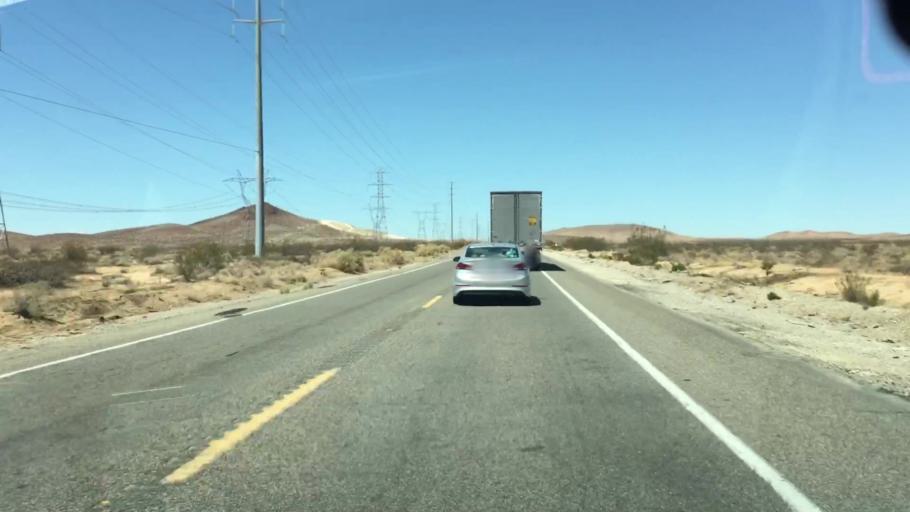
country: US
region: California
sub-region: Kern County
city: Boron
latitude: 34.8533
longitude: -117.5031
